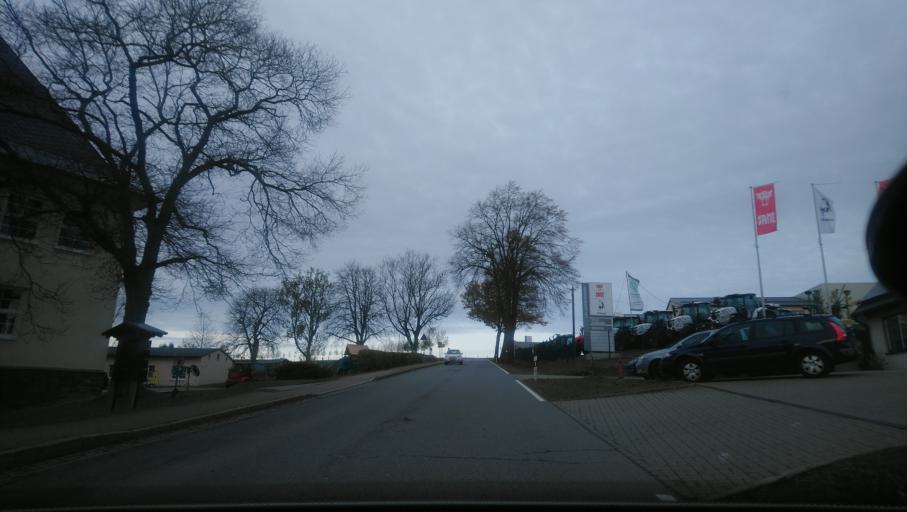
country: DE
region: Saxony
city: Hormersdorf
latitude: 50.6709
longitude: 12.8813
